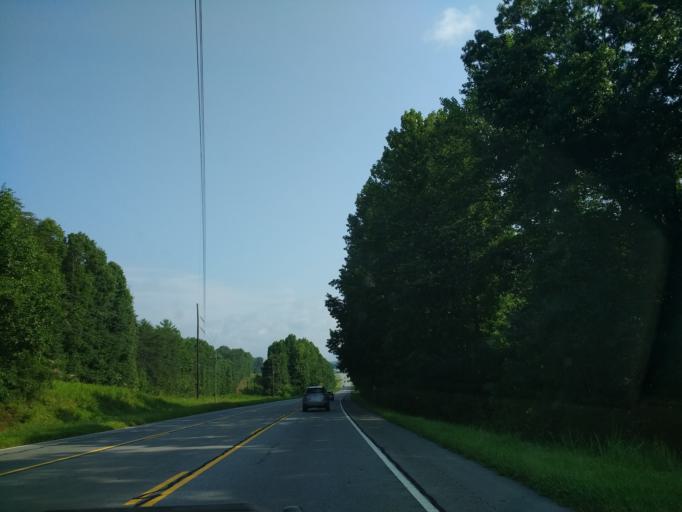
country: US
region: Georgia
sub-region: White County
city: Cleveland
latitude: 34.5465
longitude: -83.7605
